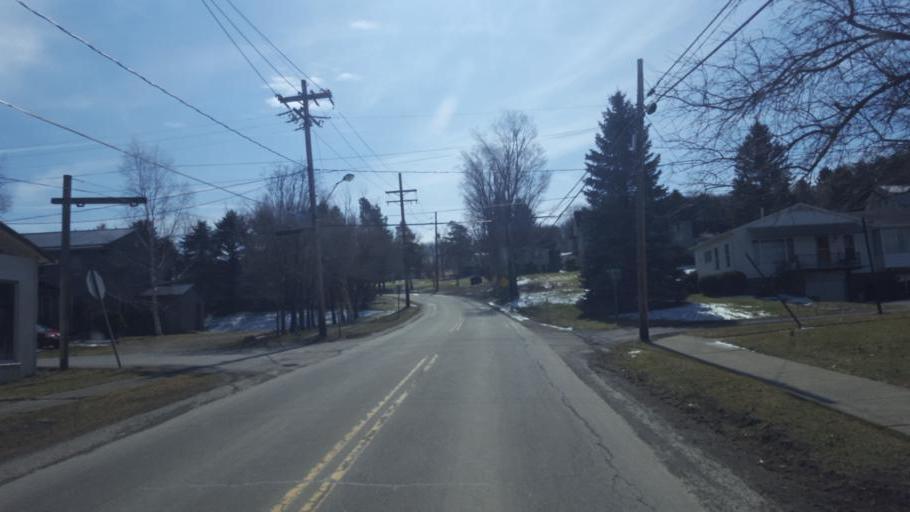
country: US
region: Pennsylvania
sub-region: Potter County
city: Galeton
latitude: 41.8994
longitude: -77.7622
